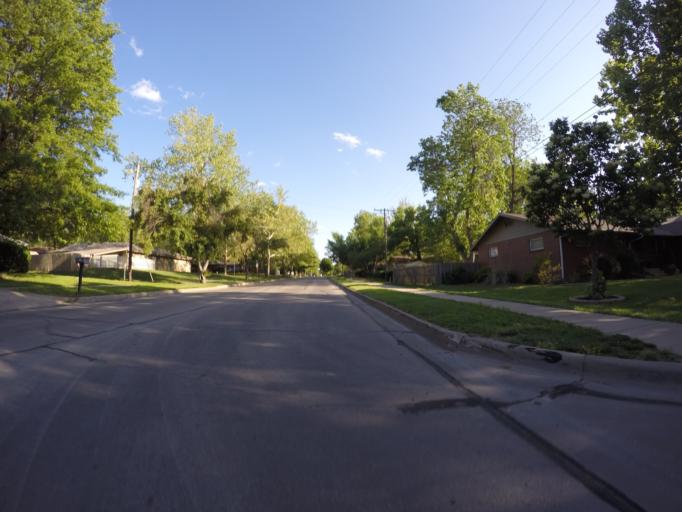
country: US
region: Kansas
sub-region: Riley County
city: Manhattan
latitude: 39.2031
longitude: -96.6075
